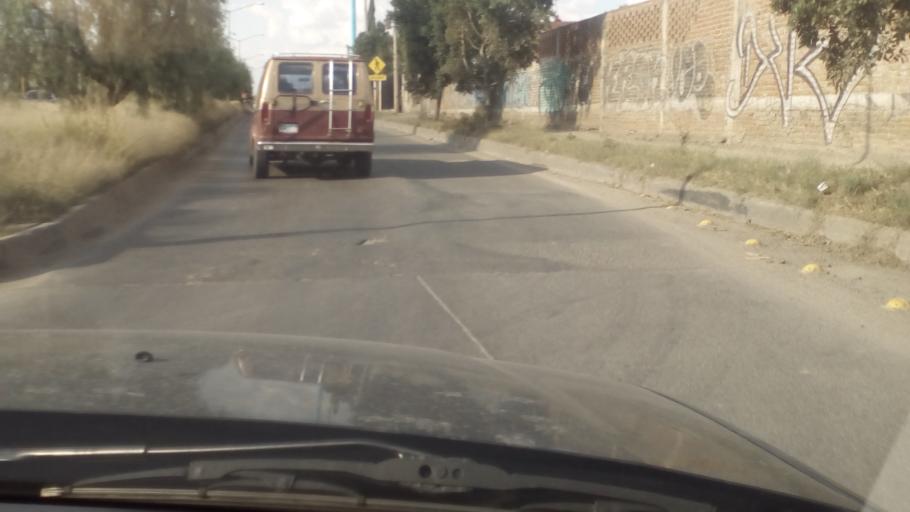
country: MX
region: Guanajuato
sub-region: Leon
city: La Ermita
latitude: 21.1436
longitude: -101.7262
